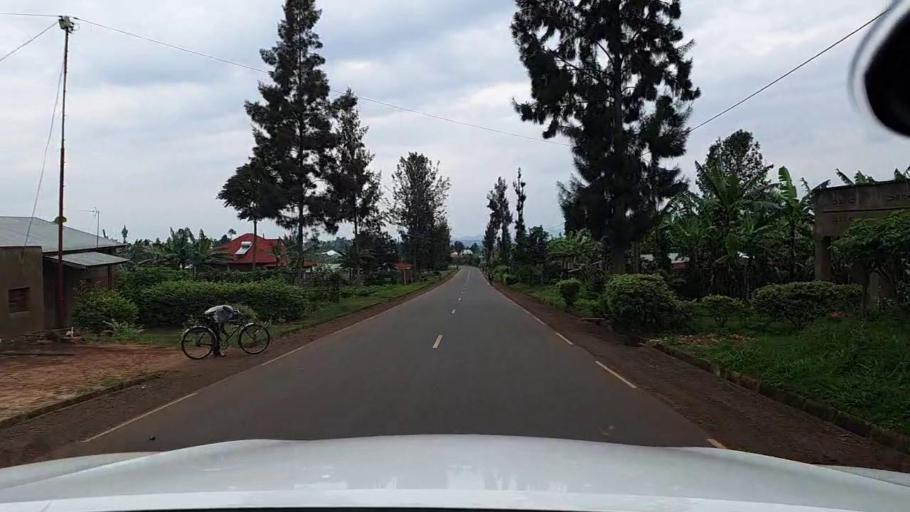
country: RW
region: Western Province
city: Cyangugu
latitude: -2.6012
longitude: 28.9329
